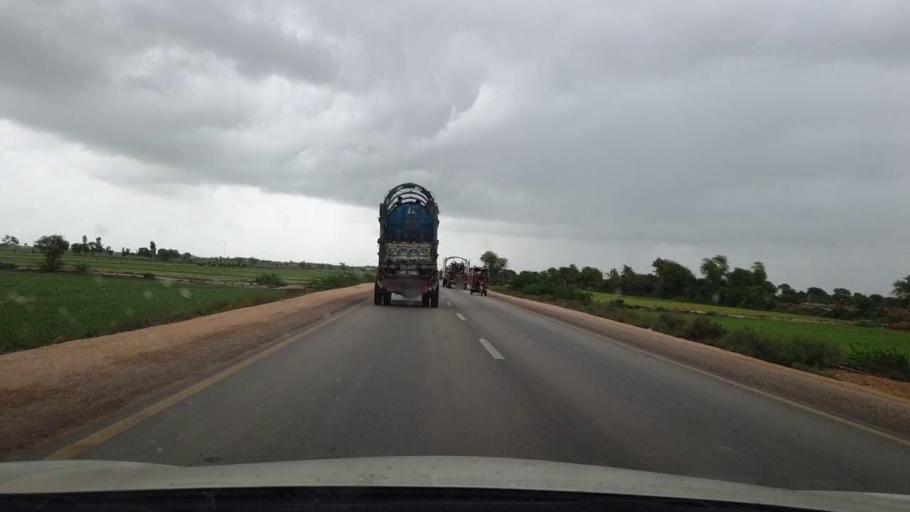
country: PK
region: Sindh
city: Kario
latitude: 24.6450
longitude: 68.4832
